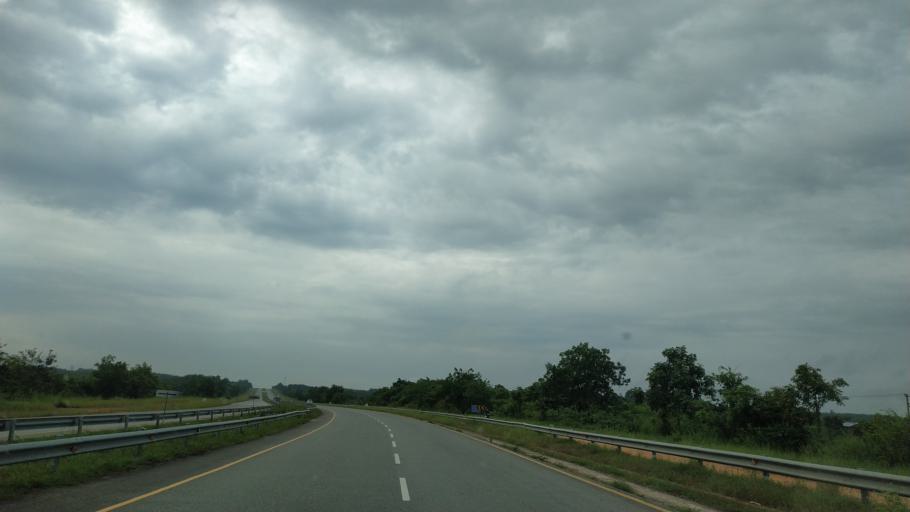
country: MM
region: Bago
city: Thanatpin
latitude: 17.3274
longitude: 96.2119
